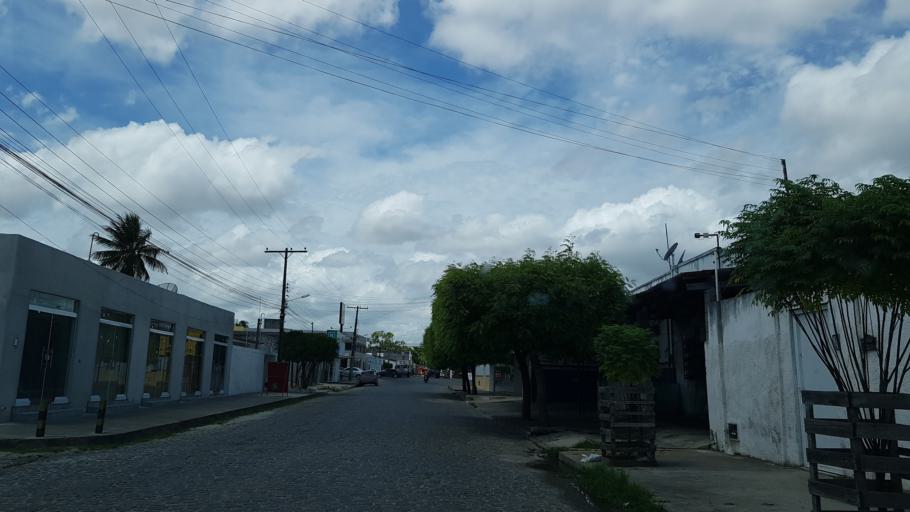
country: BR
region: Alagoas
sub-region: Penedo
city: Penedo
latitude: -10.2826
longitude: -36.5628
